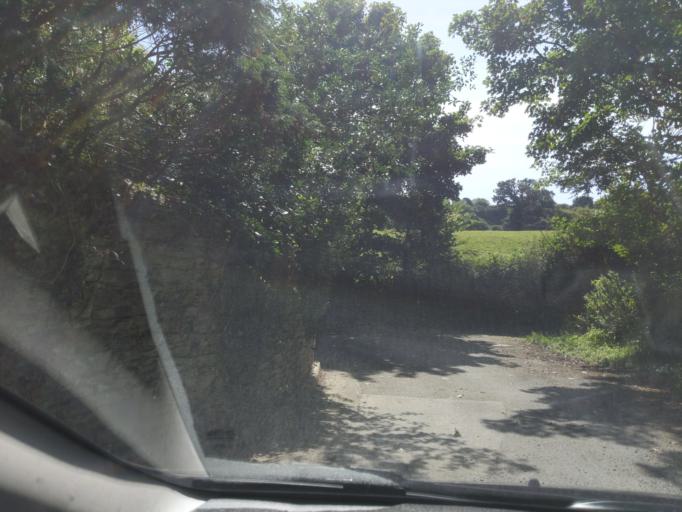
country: GB
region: England
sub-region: Devon
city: Plympton
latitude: 50.3825
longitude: -4.0520
